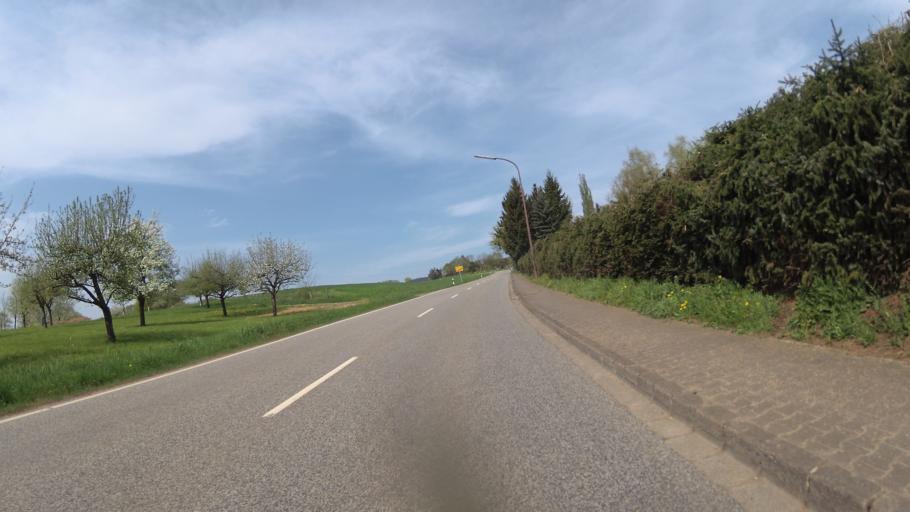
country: DE
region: Rheinland-Pfalz
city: Kinderbeuern
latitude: 50.0120
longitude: 7.0218
